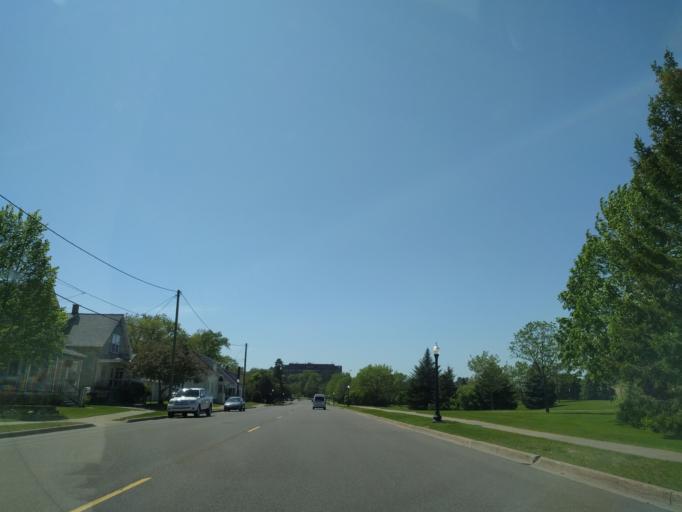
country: US
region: Michigan
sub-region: Marquette County
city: Marquette
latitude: 46.5566
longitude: -87.3910
